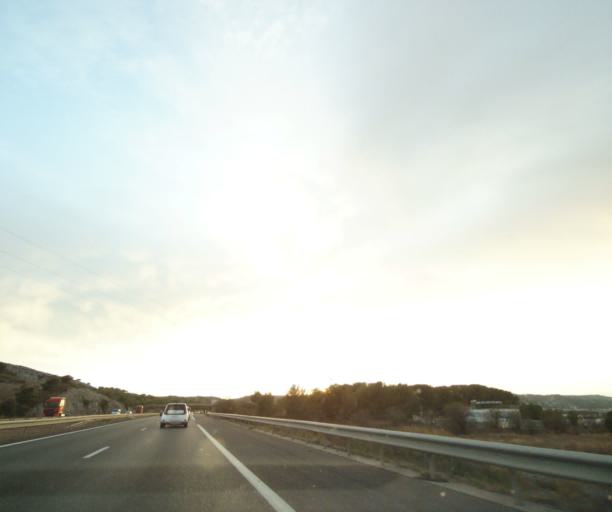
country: FR
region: Provence-Alpes-Cote d'Azur
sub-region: Departement des Bouches-du-Rhone
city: Ensues-la-Redonne
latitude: 43.3773
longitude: 5.2020
